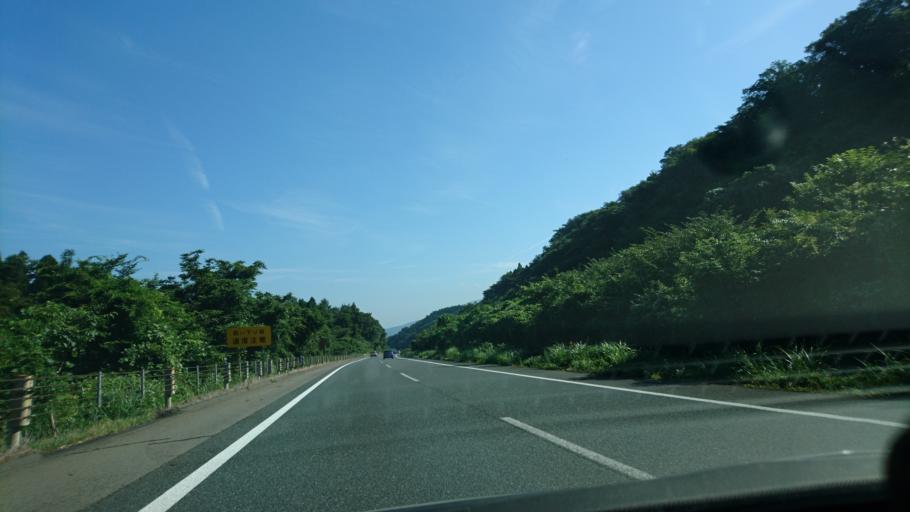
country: JP
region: Iwate
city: Ichinoseki
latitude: 38.9584
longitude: 141.1081
